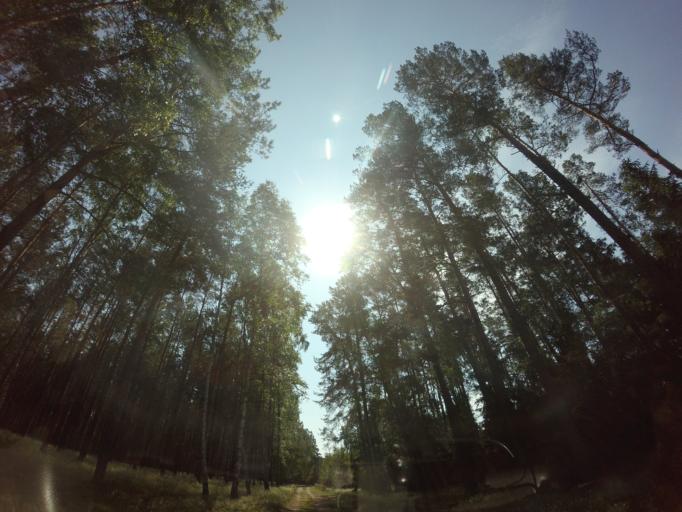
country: PL
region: West Pomeranian Voivodeship
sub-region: Powiat choszczenski
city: Bierzwnik
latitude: 53.1038
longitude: 15.7076
